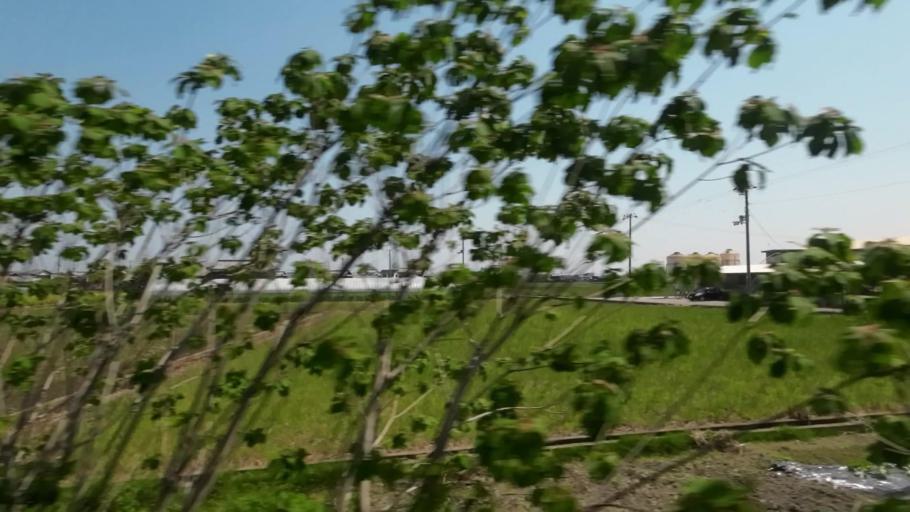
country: JP
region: Ehime
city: Saijo
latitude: 33.9227
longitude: 133.0918
